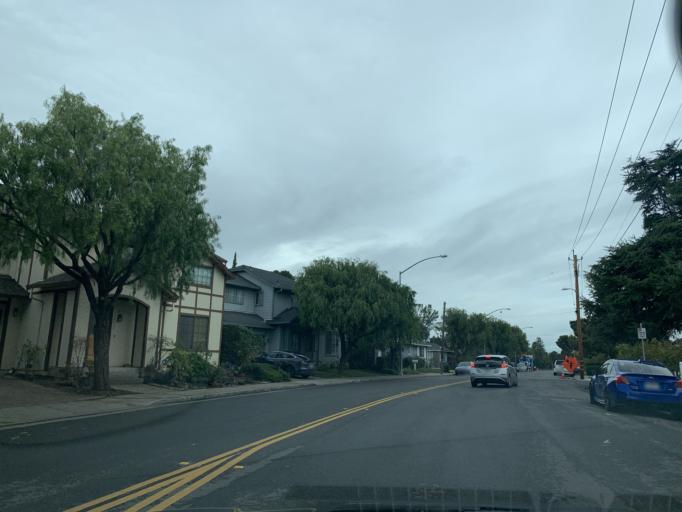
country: US
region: California
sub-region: Santa Clara County
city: Cupertino
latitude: 37.3236
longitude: -122.0527
